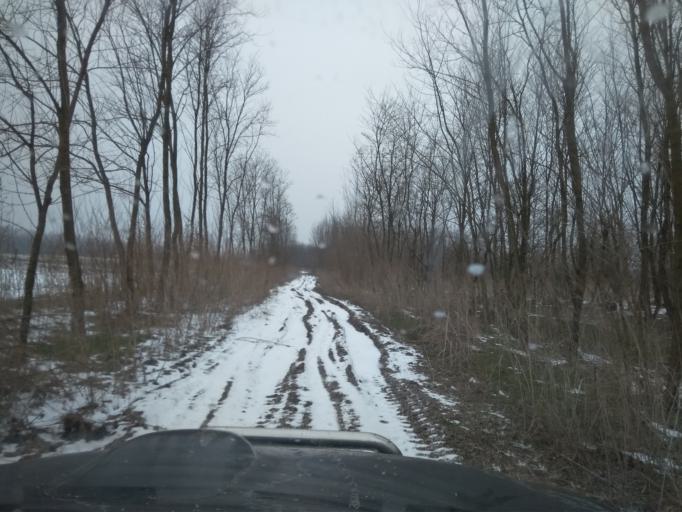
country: HU
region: Szabolcs-Szatmar-Bereg
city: Apagy
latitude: 47.9818
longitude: 21.9108
